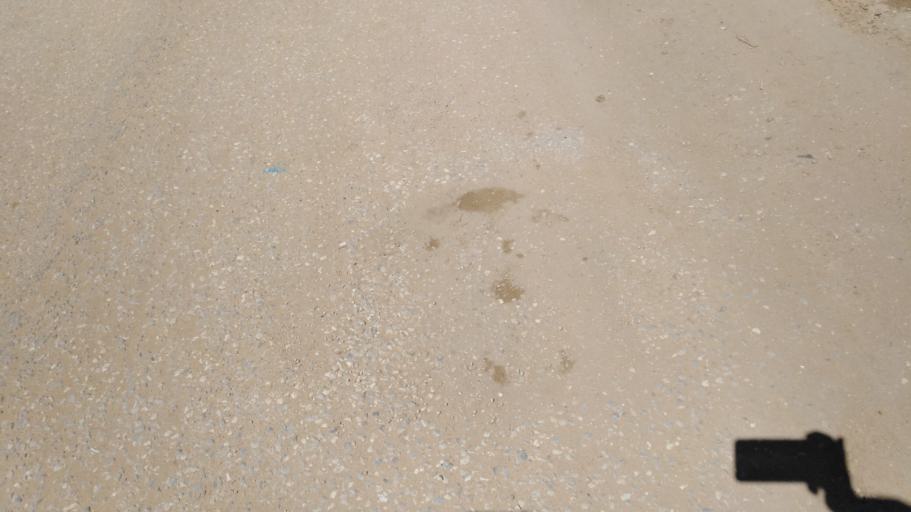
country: TN
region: Safaqis
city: Sfax
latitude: 34.7427
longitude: 10.5298
